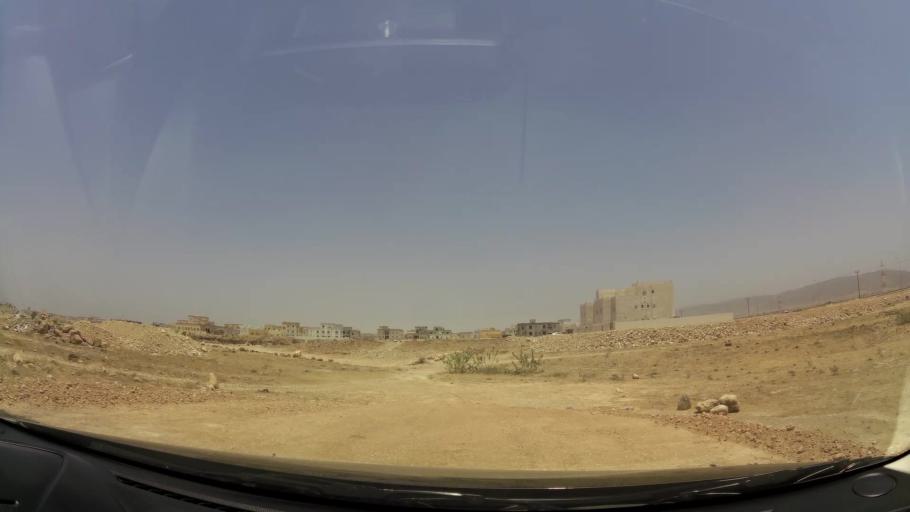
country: OM
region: Zufar
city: Salalah
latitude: 17.1003
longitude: 54.1654
